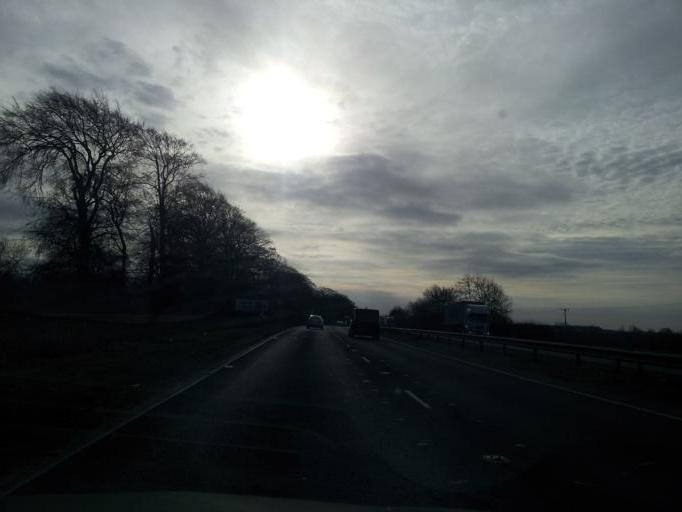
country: GB
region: England
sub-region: Lincolnshire
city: Stamford
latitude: 52.6269
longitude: -0.4656
